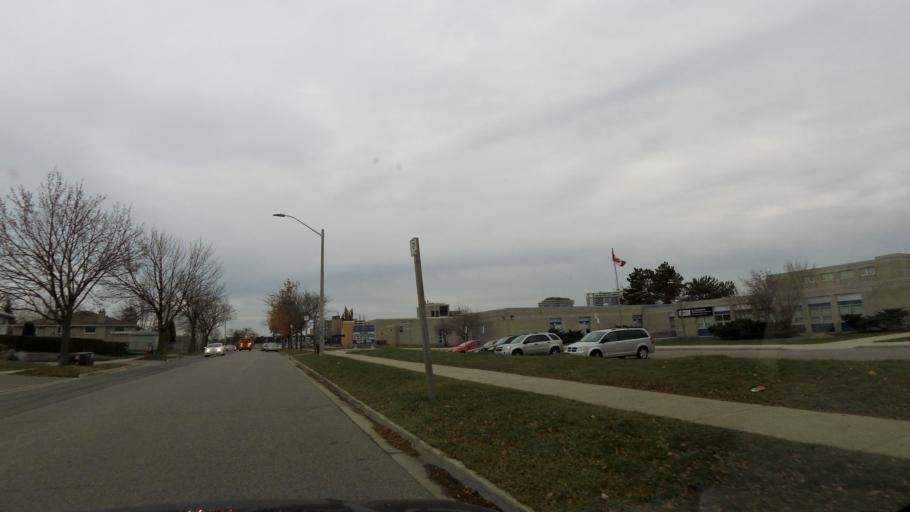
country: CA
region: Ontario
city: Etobicoke
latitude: 43.6231
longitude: -79.5974
